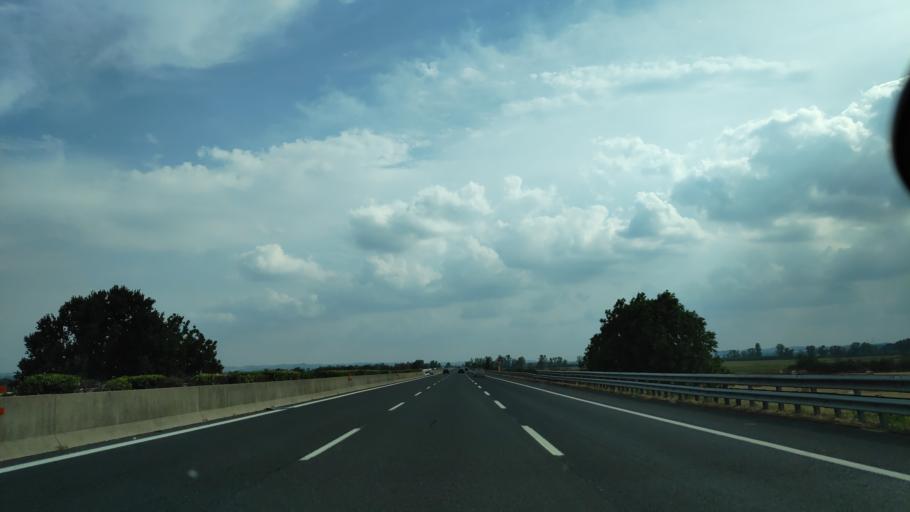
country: IT
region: Latium
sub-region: Citta metropolitana di Roma Capitale
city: Fiano Romano
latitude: 42.1436
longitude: 12.6220
